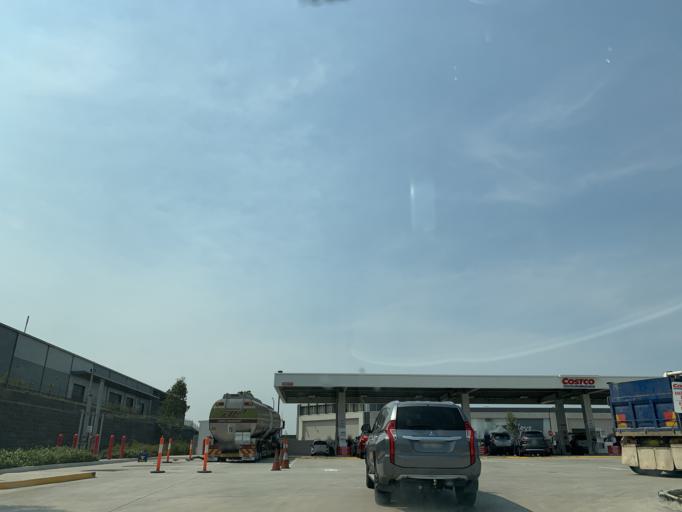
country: AU
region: New South Wales
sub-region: Blacktown
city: Hassall Grove
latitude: -33.7217
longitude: 150.8397
